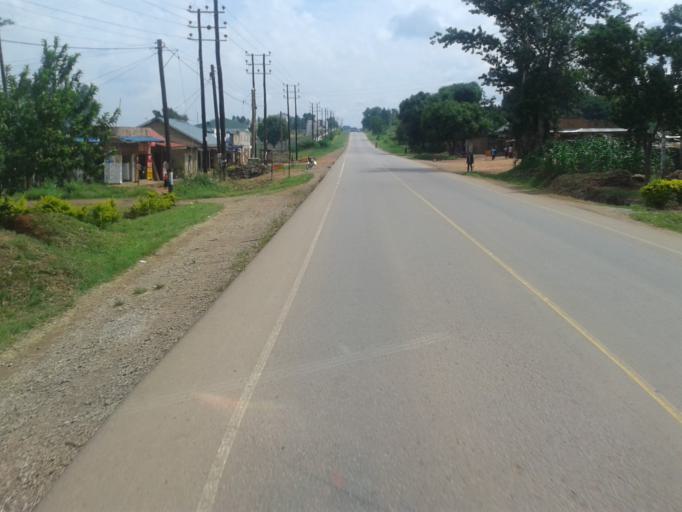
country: UG
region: Central Region
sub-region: Wakiso District
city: Wakiso
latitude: 0.5353
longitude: 32.5301
